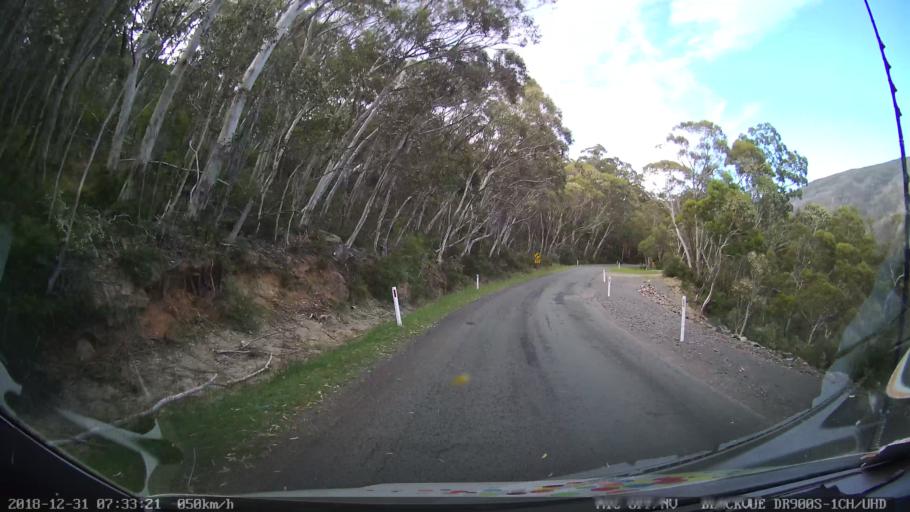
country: AU
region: New South Wales
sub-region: Snowy River
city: Jindabyne
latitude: -36.3324
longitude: 148.4579
